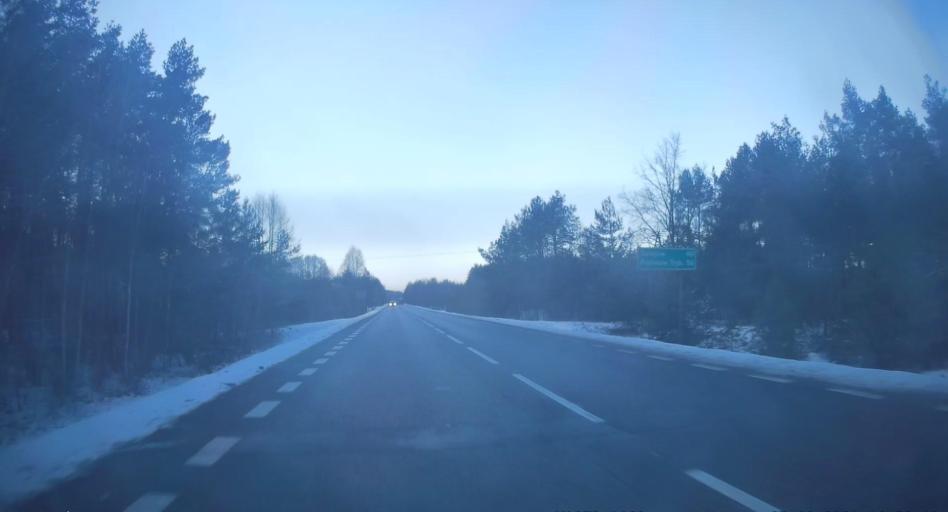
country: PL
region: Swietokrzyskie
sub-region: Powiat konecki
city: Ruda Maleniecka
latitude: 51.1279
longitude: 20.2551
